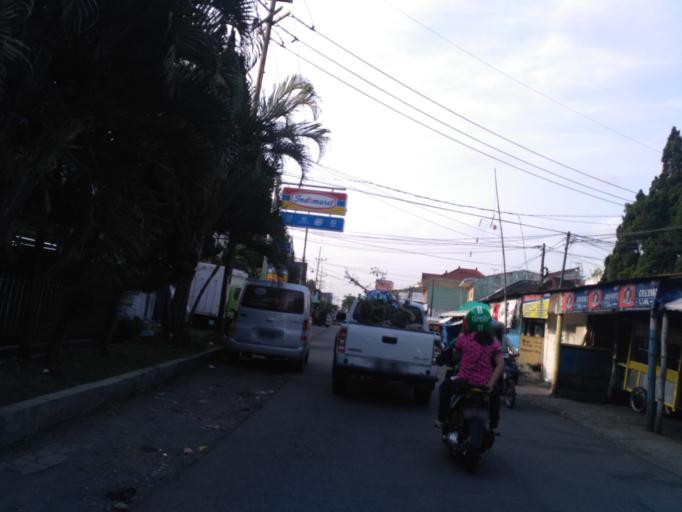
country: ID
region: East Java
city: Malang
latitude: -7.9389
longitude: 112.6370
